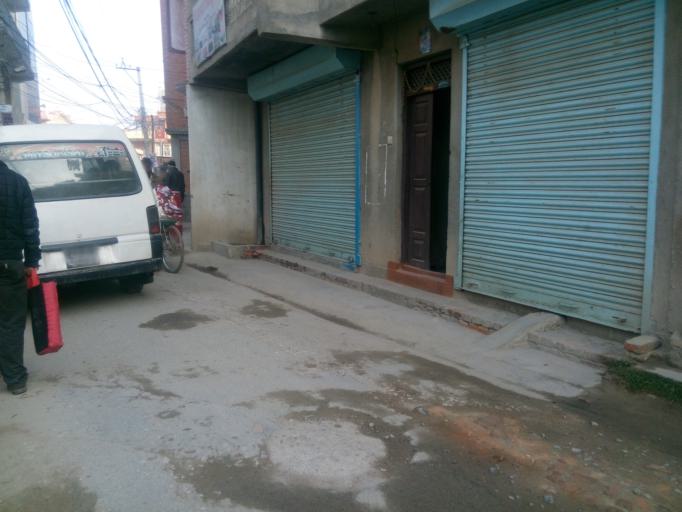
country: NP
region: Central Region
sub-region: Bagmati Zone
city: Patan
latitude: 27.6631
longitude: 85.3366
